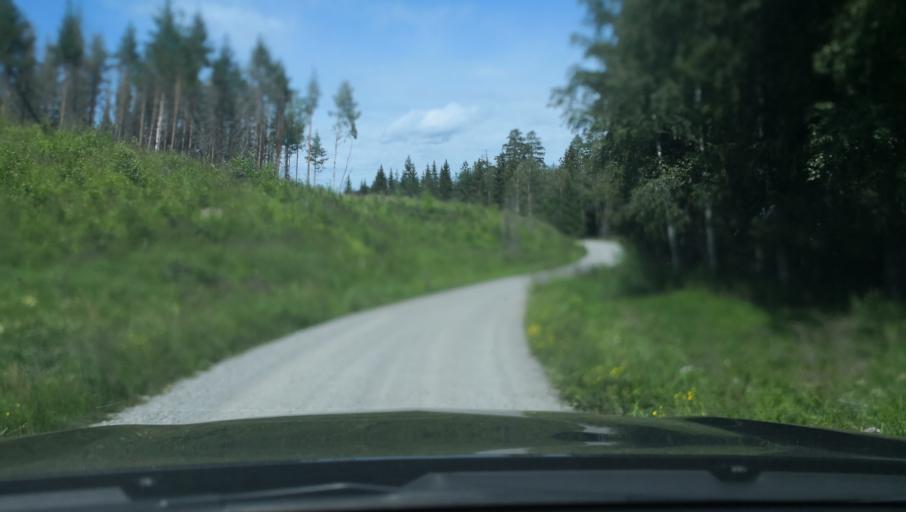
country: SE
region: Vaestmanland
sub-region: Surahammars Kommun
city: Ramnas
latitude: 59.8901
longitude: 16.0992
